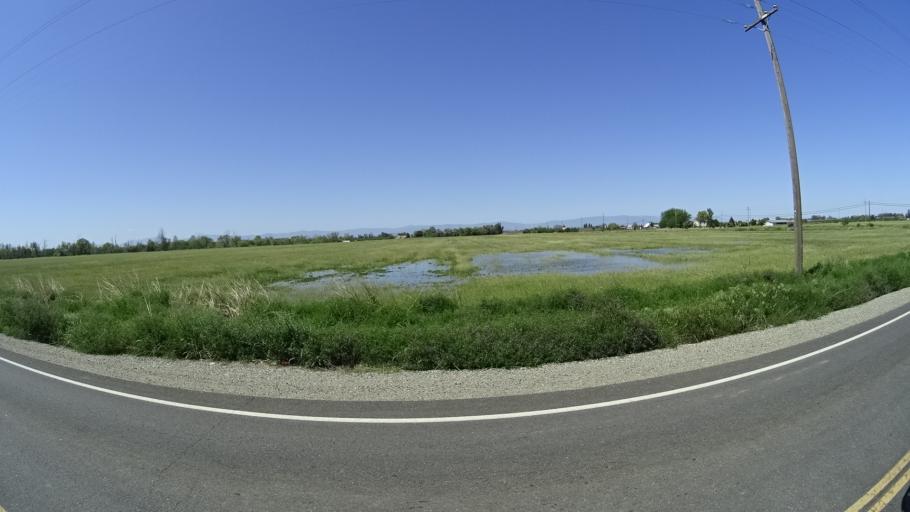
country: US
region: California
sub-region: Glenn County
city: Orland
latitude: 39.7672
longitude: -122.1409
